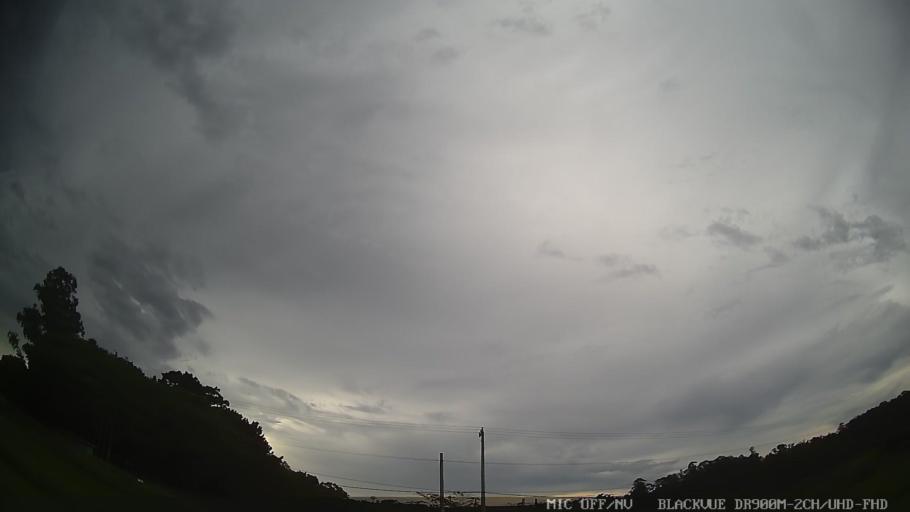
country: BR
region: Sao Paulo
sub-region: Jaguariuna
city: Jaguariuna
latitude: -22.7255
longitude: -47.0146
